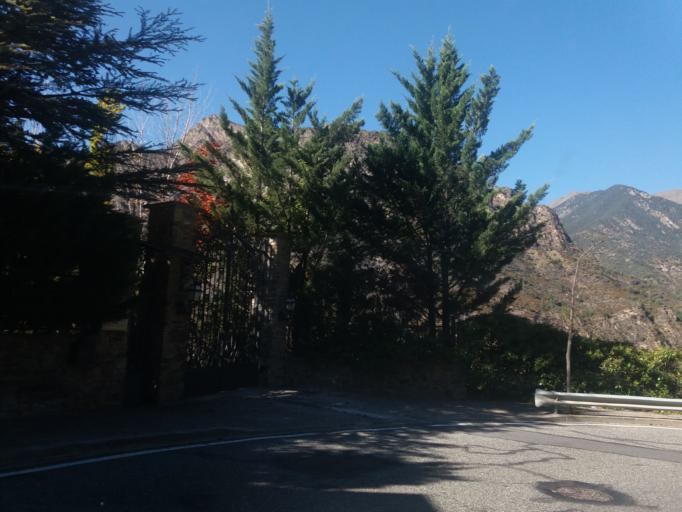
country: AD
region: Sant Julia de Loria
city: Sant Julia de Loria
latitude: 42.4607
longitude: 1.4945
